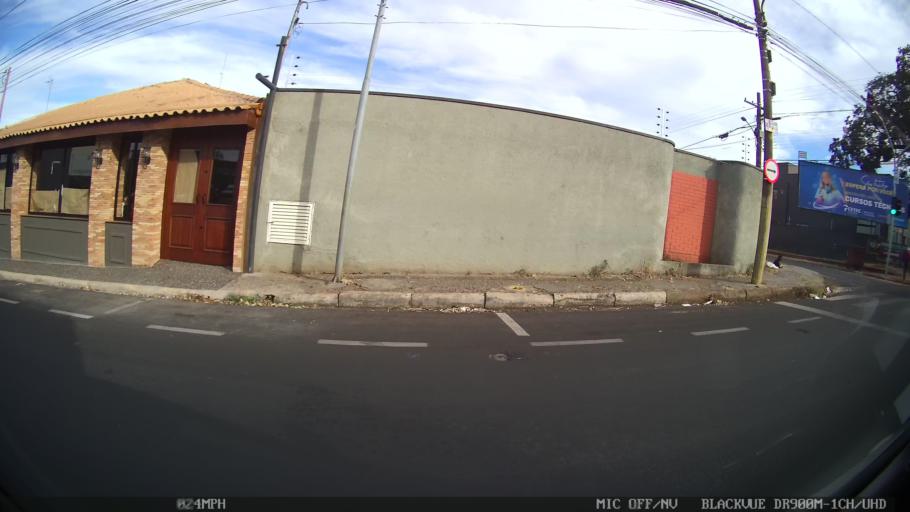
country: BR
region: Sao Paulo
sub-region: Catanduva
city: Catanduva
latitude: -21.1246
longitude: -48.9676
